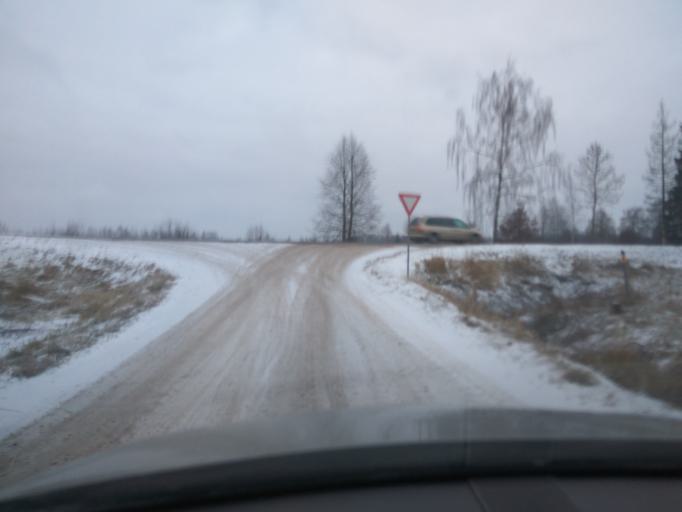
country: LV
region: Aizpute
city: Aizpute
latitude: 56.7325
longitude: 21.6665
